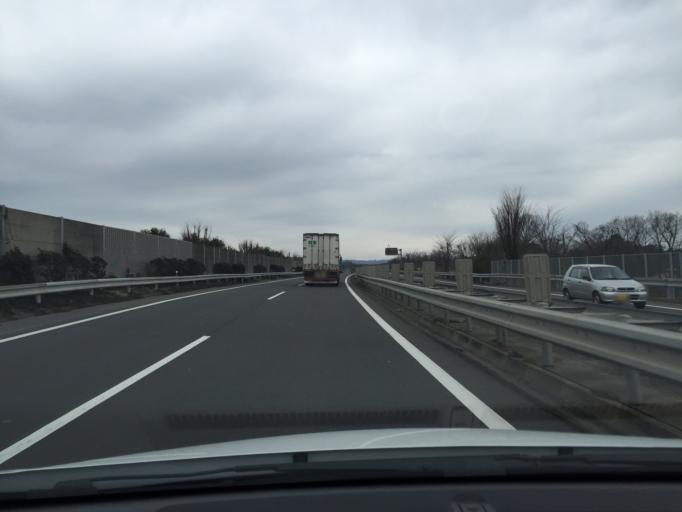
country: JP
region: Saitama
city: Sayama
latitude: 35.8606
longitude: 139.3762
